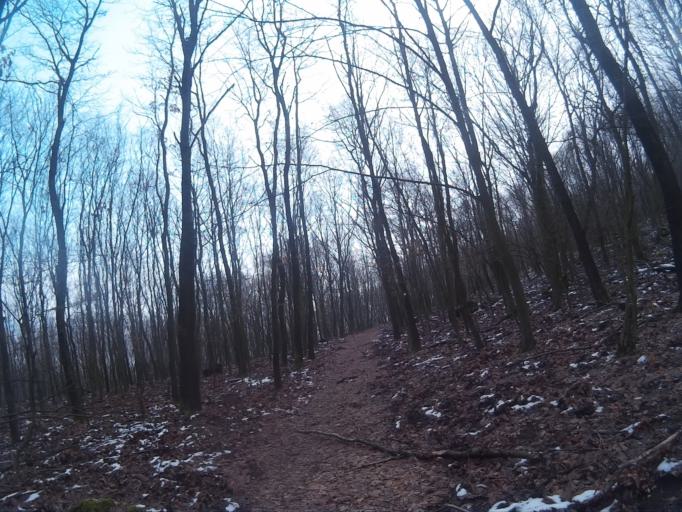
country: HU
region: Komarom-Esztergom
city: Tardos
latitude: 47.6412
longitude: 18.4774
